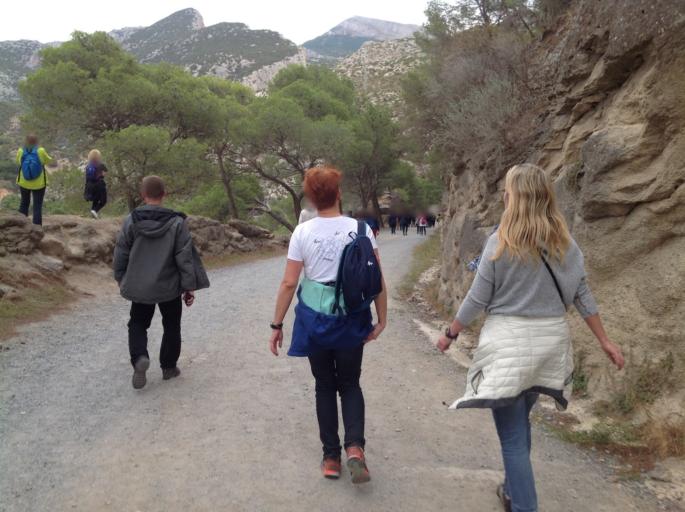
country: ES
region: Andalusia
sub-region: Provincia de Malaga
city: Ardales
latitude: 36.9296
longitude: -4.7964
